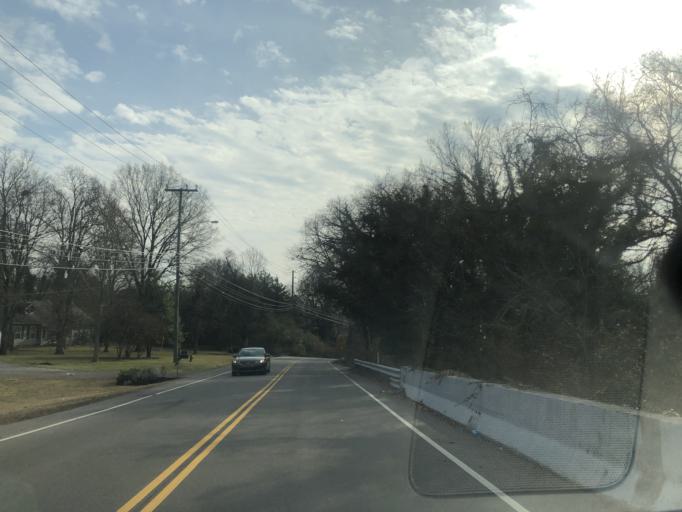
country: US
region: Tennessee
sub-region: Davidson County
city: Oak Hill
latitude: 36.1110
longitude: -86.7093
